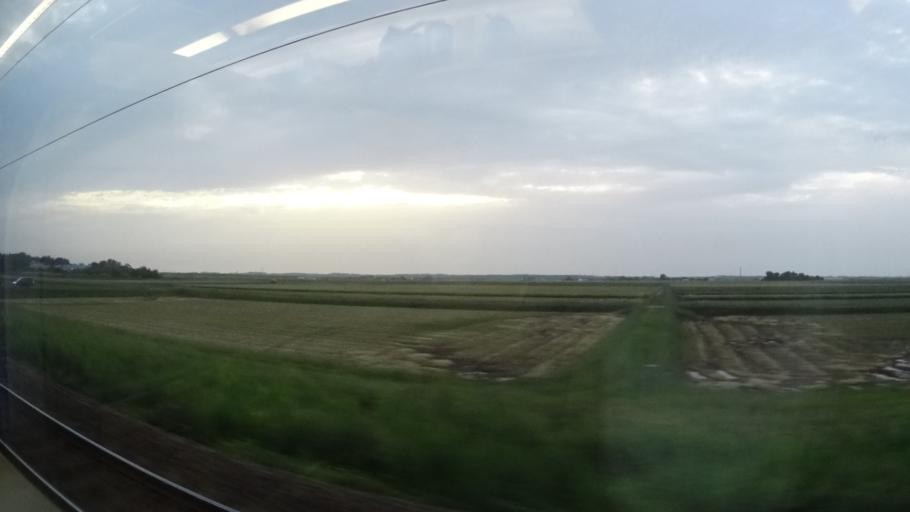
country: JP
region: Niigata
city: Murakami
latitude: 38.1120
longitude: 139.4397
